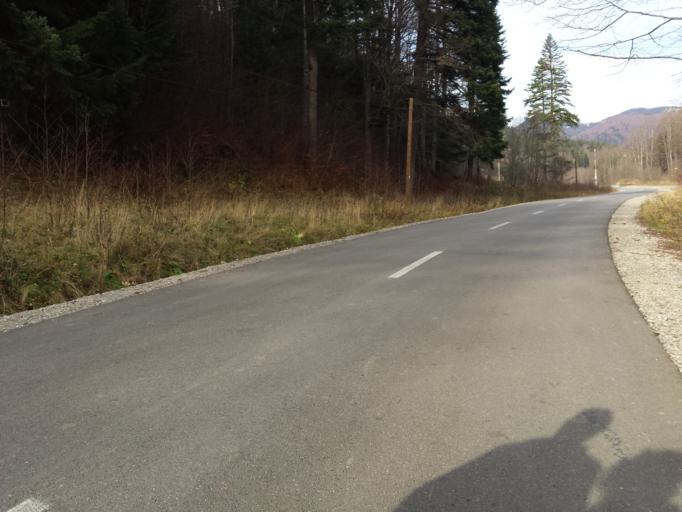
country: RO
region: Prahova
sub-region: Oras Azuga
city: Azuga
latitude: 45.4280
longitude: 25.5368
